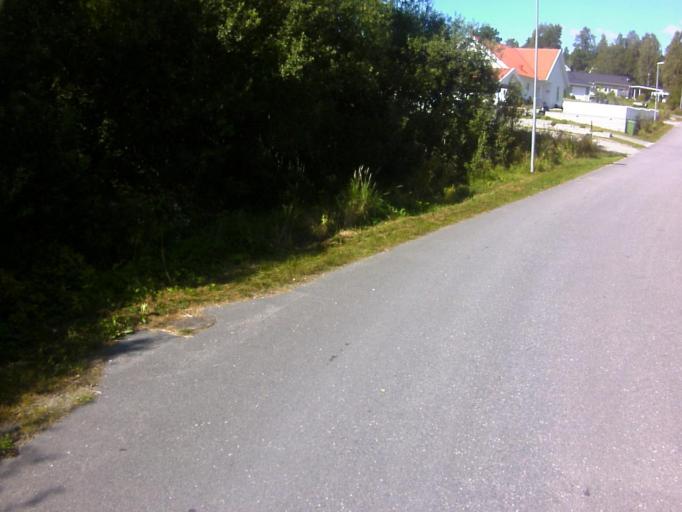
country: SE
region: Soedermanland
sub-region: Eskilstuna Kommun
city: Hallbybrunn
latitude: 59.3436
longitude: 16.4227
